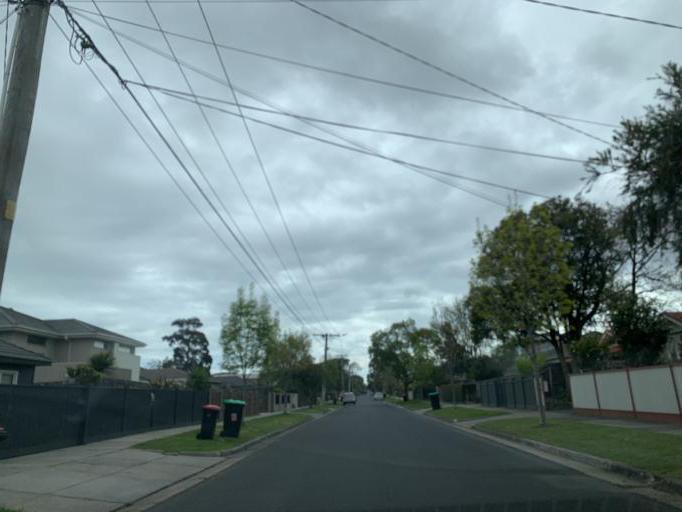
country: AU
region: Victoria
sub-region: Kingston
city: Mentone
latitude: -37.9700
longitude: 145.0663
